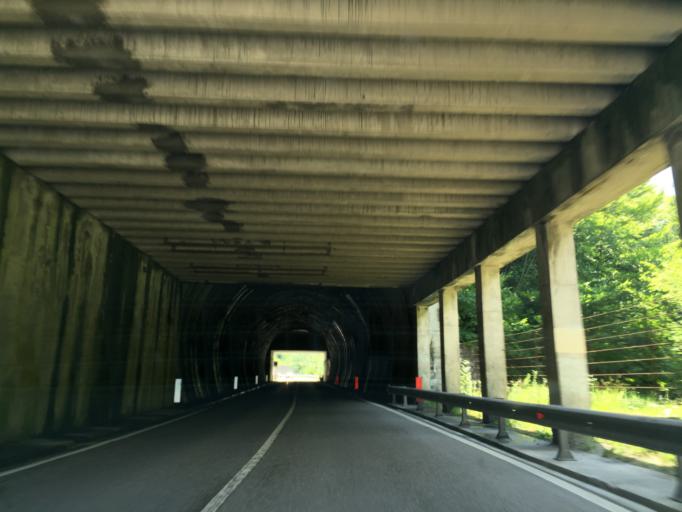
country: IT
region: Trentino-Alto Adige
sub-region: Provincia di Trento
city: Imer
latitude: 46.1139
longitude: 11.7769
